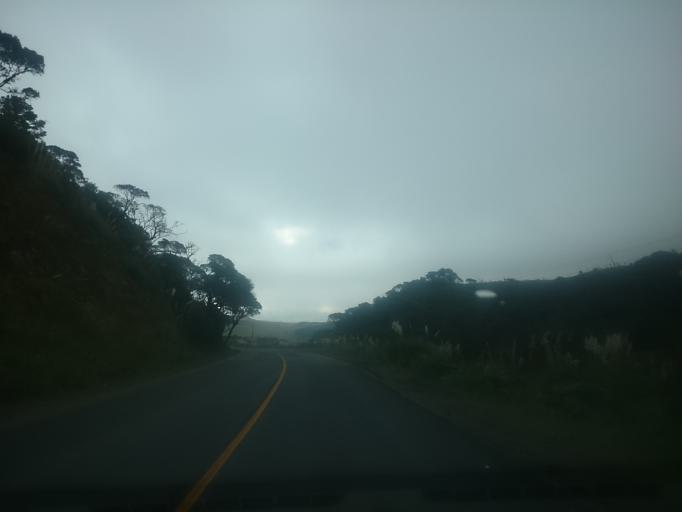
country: BR
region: Santa Catarina
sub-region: Lauro Muller
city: Lauro Muller
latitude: -28.3758
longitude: -49.5602
